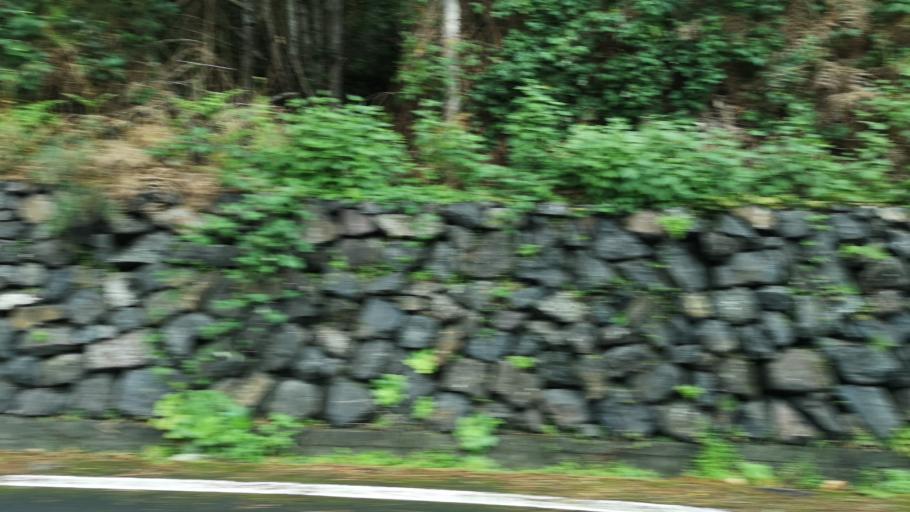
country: ES
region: Canary Islands
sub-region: Provincia de Santa Cruz de Tenerife
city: Hermigua
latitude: 28.1342
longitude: -17.1917
